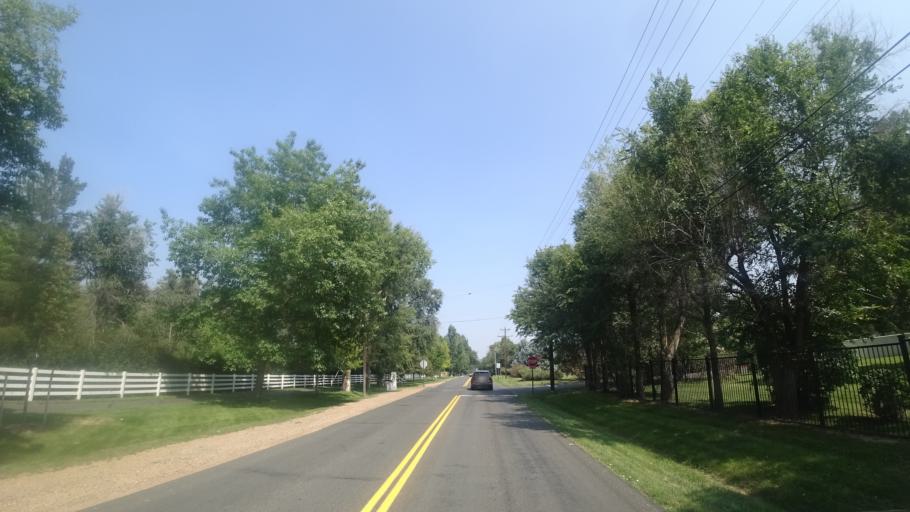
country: US
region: Colorado
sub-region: Arapahoe County
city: Cherry Hills Village
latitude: 39.6387
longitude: -104.9742
